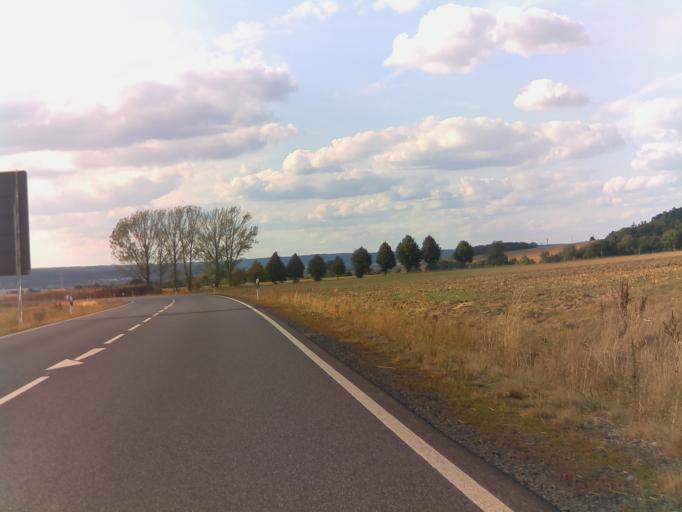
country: DE
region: Hesse
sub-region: Regierungsbezirk Kassel
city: Dipperz
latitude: 50.5417
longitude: 9.7844
